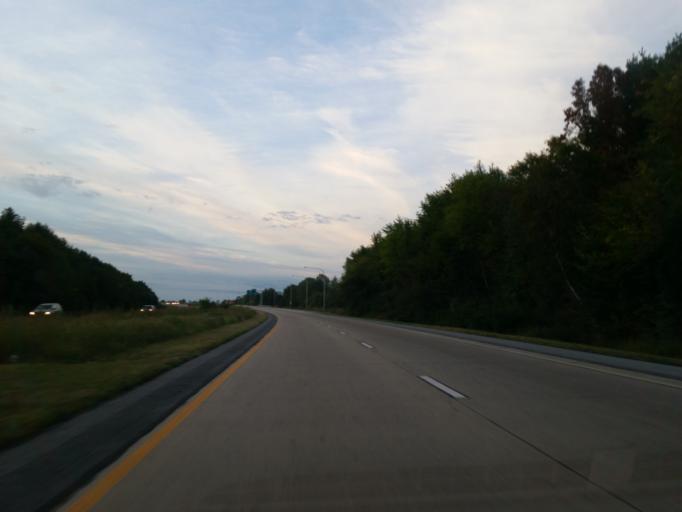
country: US
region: Delaware
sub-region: Kent County
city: Smyrna
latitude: 39.2913
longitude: -75.5936
